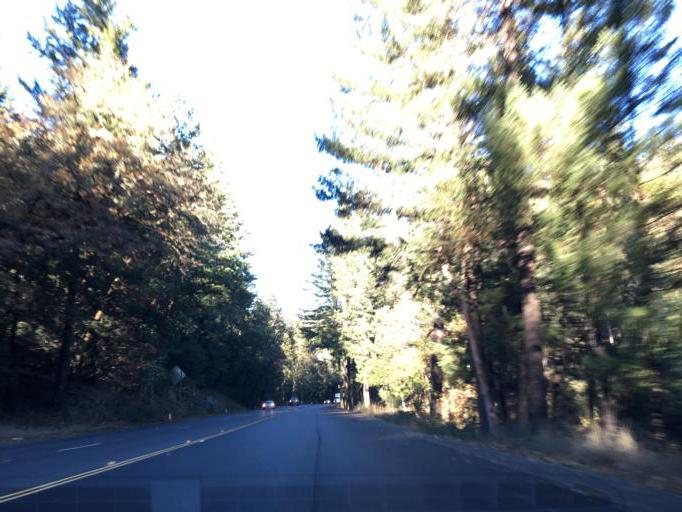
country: US
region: California
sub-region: Mendocino County
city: Laytonville
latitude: 39.7880
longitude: -123.5441
